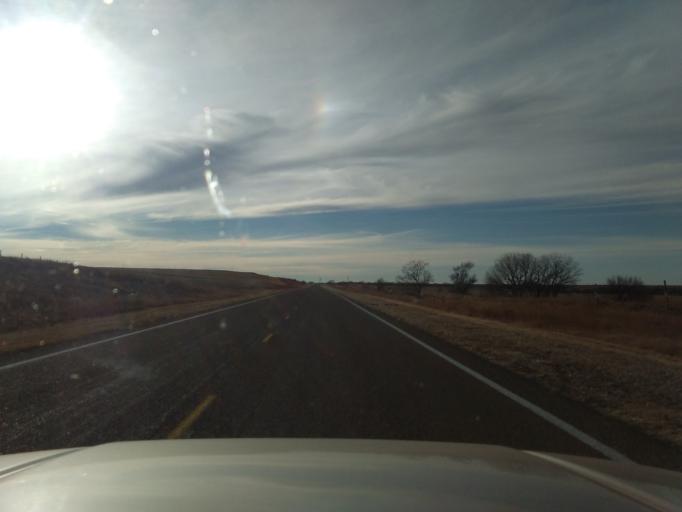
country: US
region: Kansas
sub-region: Norton County
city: Norton
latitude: 39.7501
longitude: -100.1459
